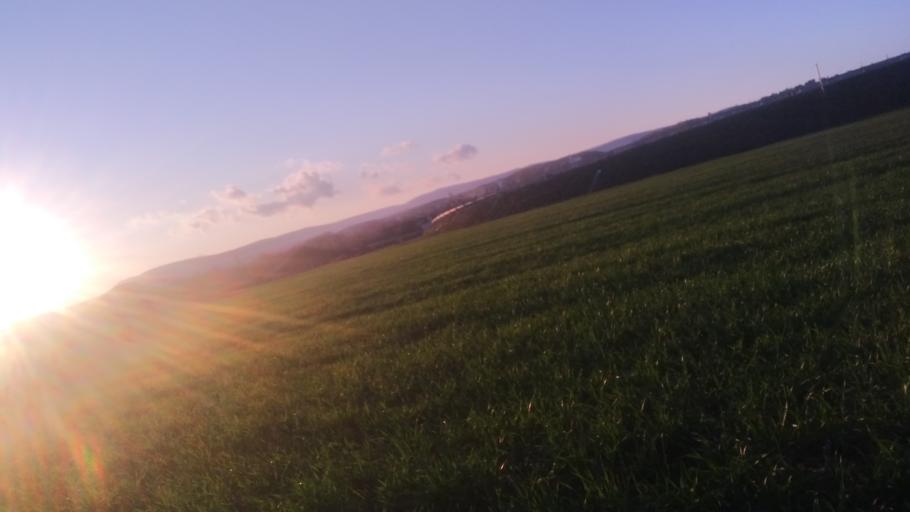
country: HU
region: Veszprem
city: Varpalota
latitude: 47.1952
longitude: 18.1873
